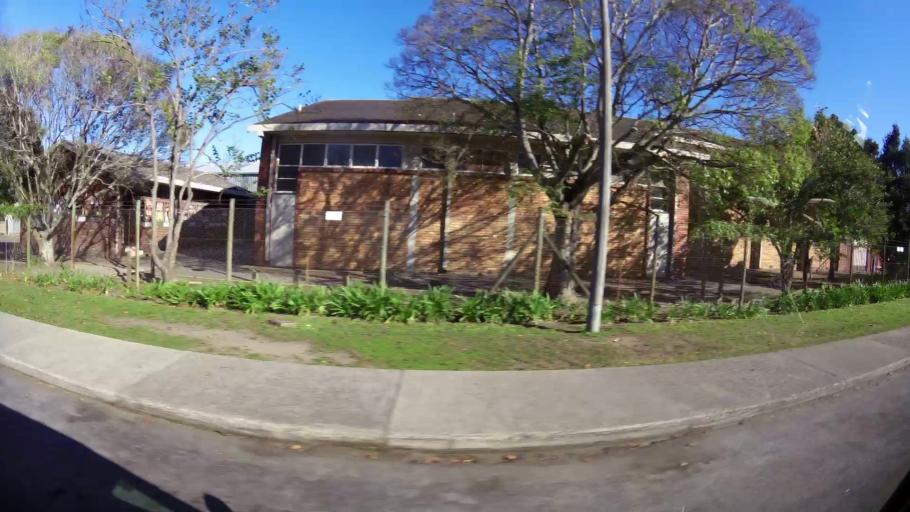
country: ZA
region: Western Cape
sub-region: Eden District Municipality
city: Knysna
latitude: -34.0390
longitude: 23.0487
